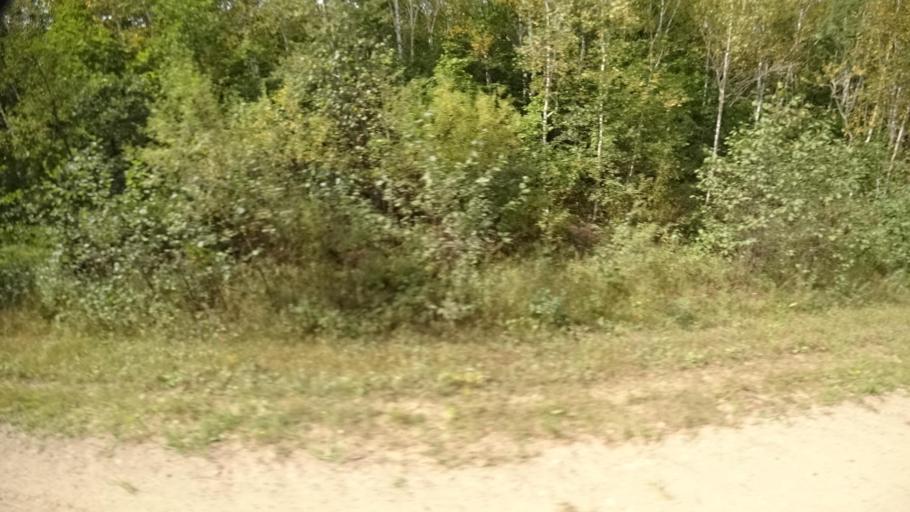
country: RU
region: Primorskiy
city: Yakovlevka
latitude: 44.6740
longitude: 133.6120
